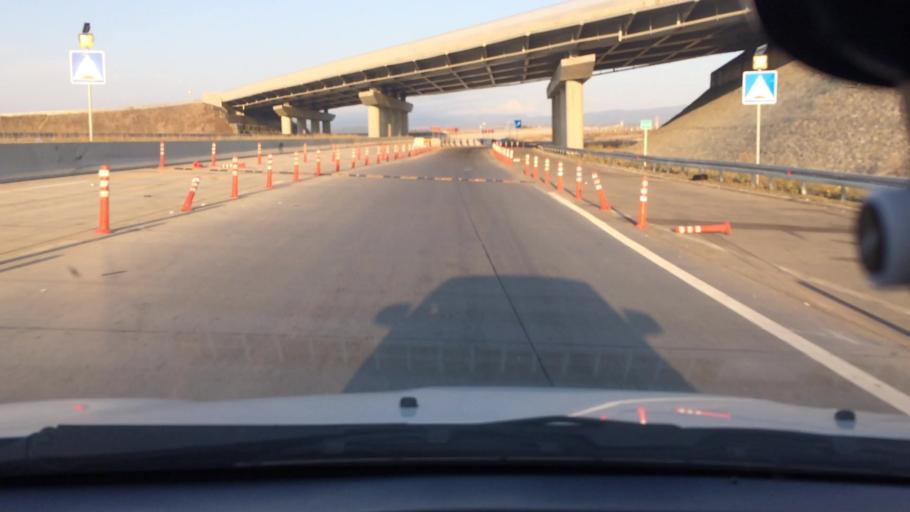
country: GE
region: Shida Kartli
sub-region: Khashuris Raioni
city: Khashuri
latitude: 42.0110
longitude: 43.7005
